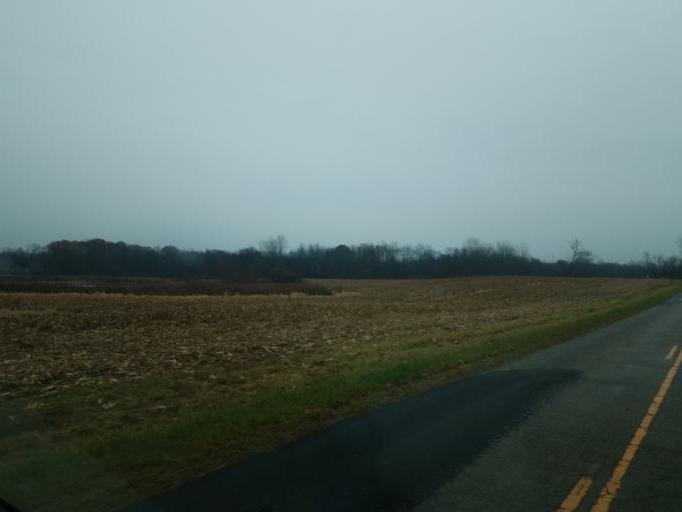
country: US
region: Ohio
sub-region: Knox County
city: Centerburg
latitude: 40.3752
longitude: -82.6355
